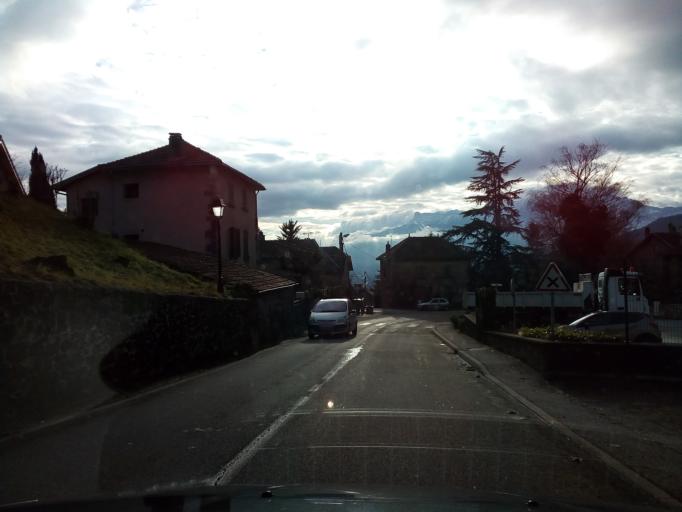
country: FR
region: Rhone-Alpes
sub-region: Departement de l'Isere
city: Corenc
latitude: 45.2194
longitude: 5.7618
